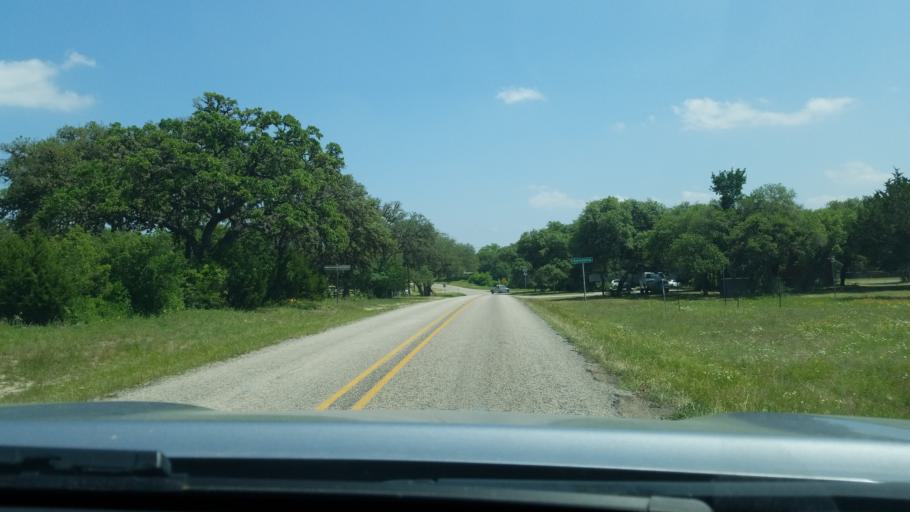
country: US
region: Texas
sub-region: Blanco County
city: Blanco
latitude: 29.9710
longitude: -98.5255
